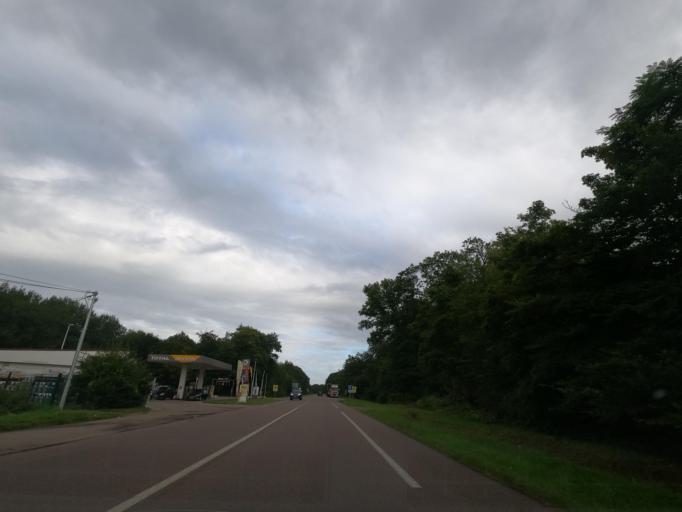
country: FR
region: Haute-Normandie
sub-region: Departement de la Seine-Maritime
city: Sahurs
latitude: 49.3436
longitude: 0.9350
